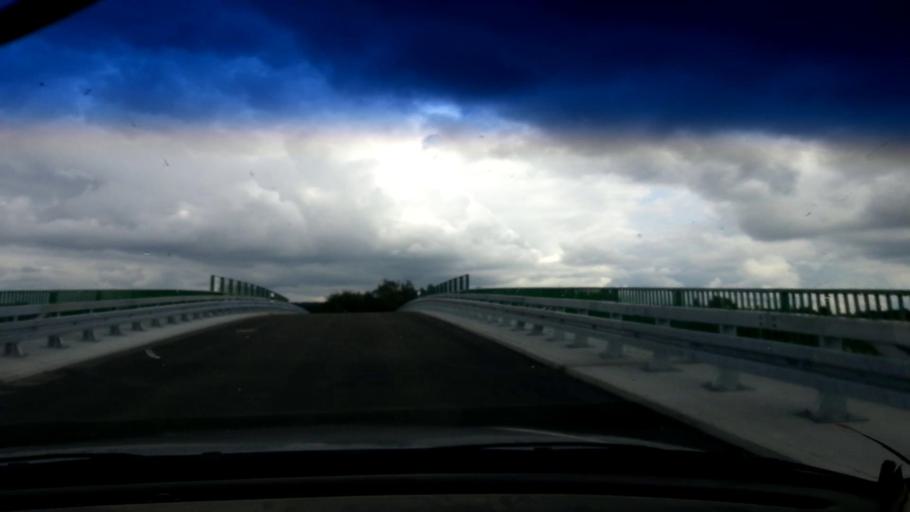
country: DE
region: Bavaria
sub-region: Upper Franconia
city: Kemmern
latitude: 49.9551
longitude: 10.8856
